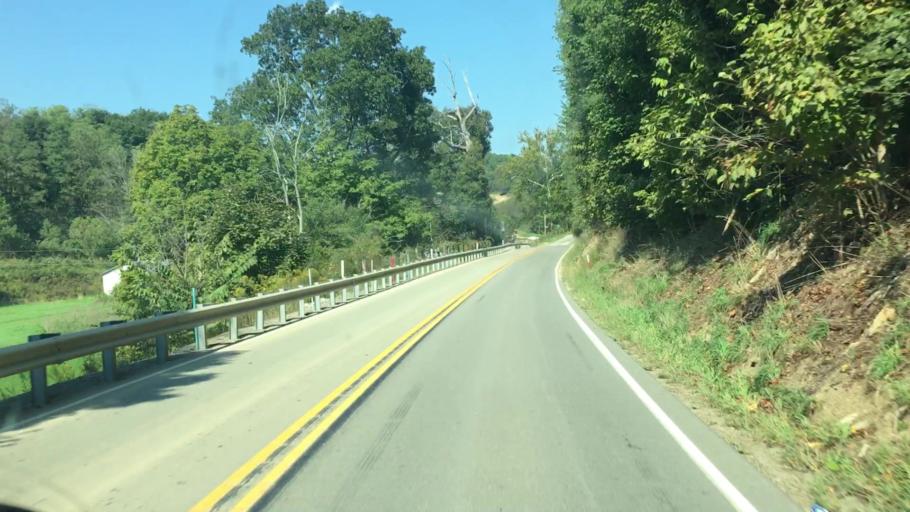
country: US
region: Pennsylvania
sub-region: Greene County
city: Waynesburg
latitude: 39.9672
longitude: -80.3161
